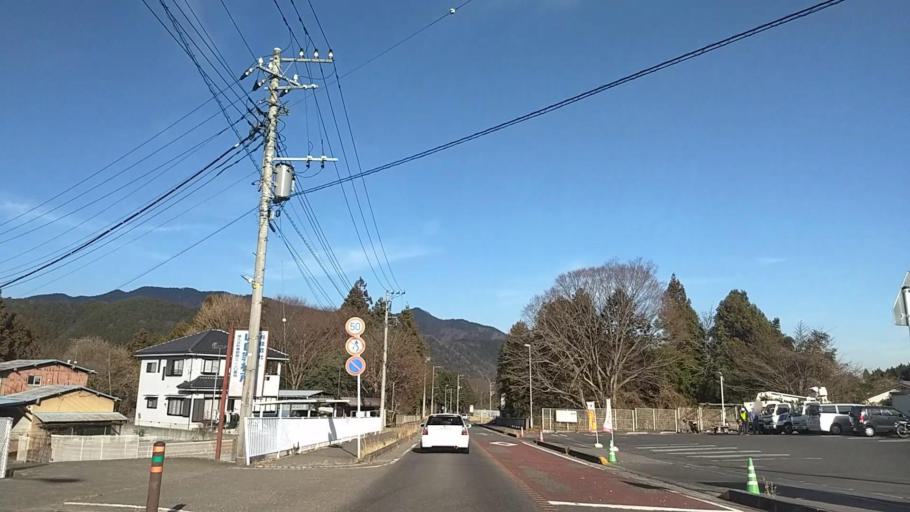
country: JP
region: Yamanashi
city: Uenohara
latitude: 35.5591
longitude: 139.1754
